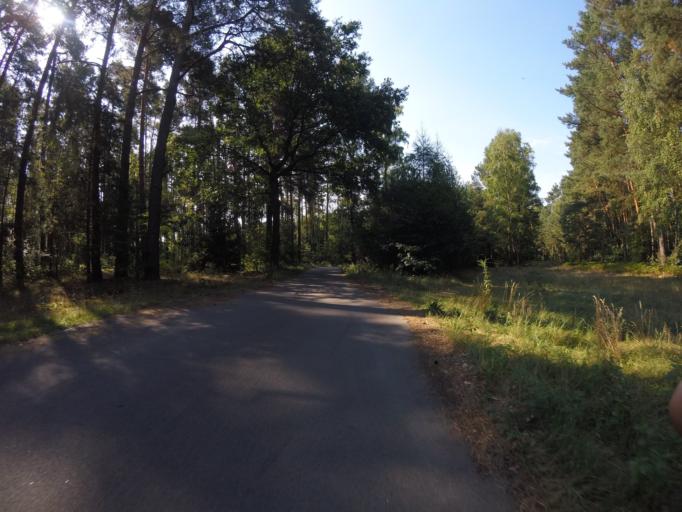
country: DE
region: Brandenburg
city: Berkenbruck
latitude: 52.3115
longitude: 14.2122
